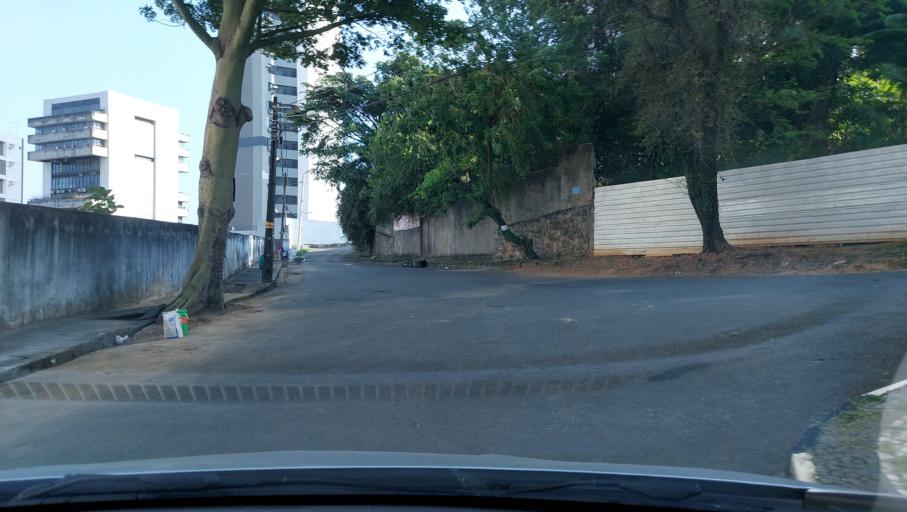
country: BR
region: Bahia
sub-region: Salvador
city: Salvador
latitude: -12.9857
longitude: -38.4681
